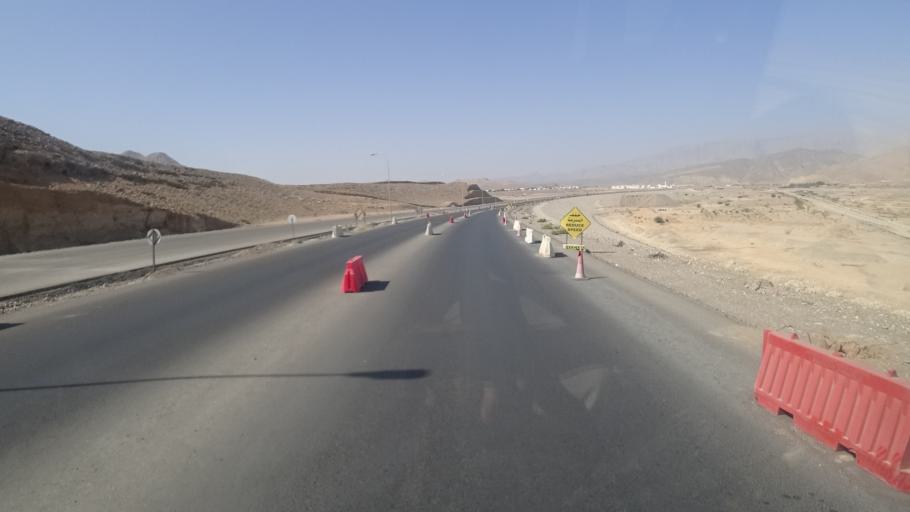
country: OM
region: Ash Sharqiyah
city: Sur
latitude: 22.5198
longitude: 59.4616
